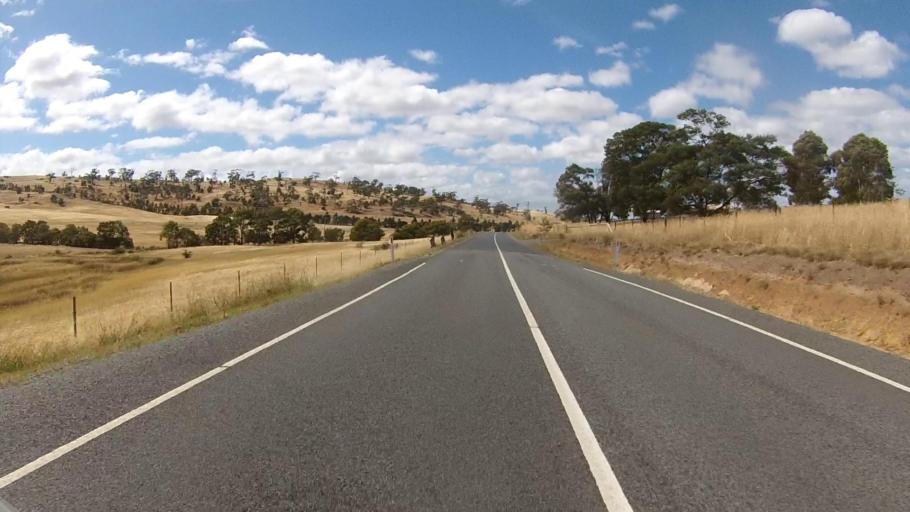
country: AU
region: Tasmania
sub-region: Sorell
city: Sorell
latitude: -42.7519
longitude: 147.4995
